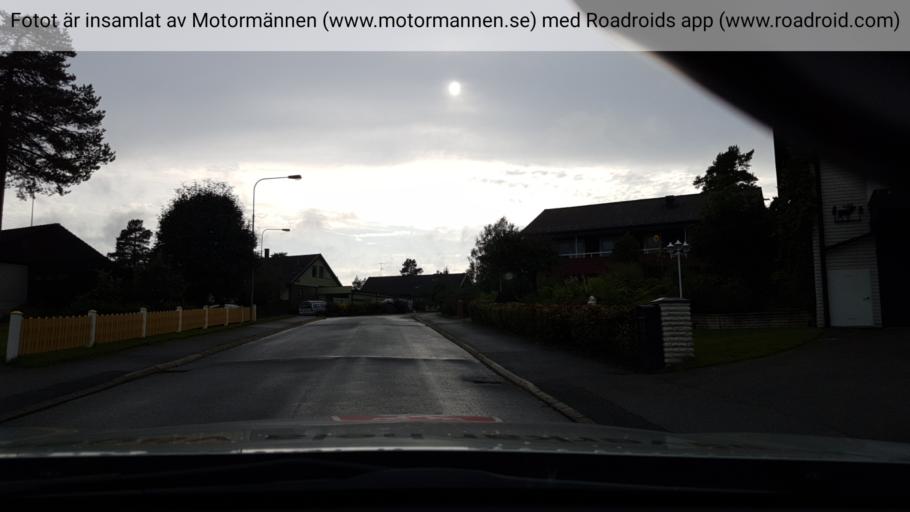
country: SE
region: Vaesterbotten
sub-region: Umea Kommun
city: Saevar
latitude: 63.8984
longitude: 20.5374
